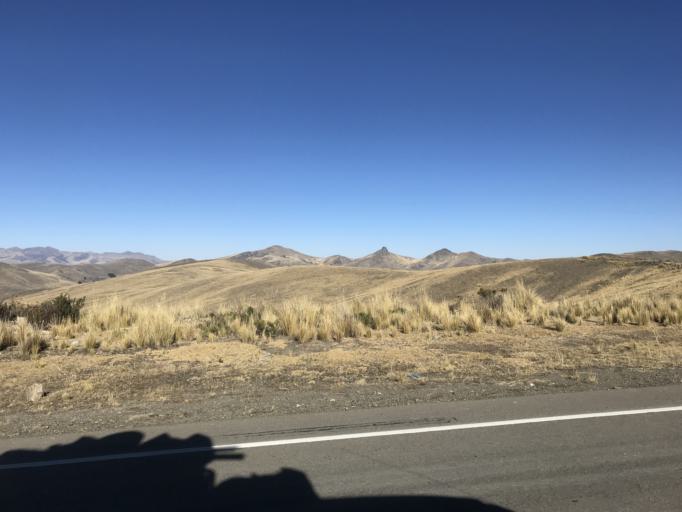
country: PE
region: Puno
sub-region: Yunguyo
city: Yunguyo
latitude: -16.1641
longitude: -68.9865
